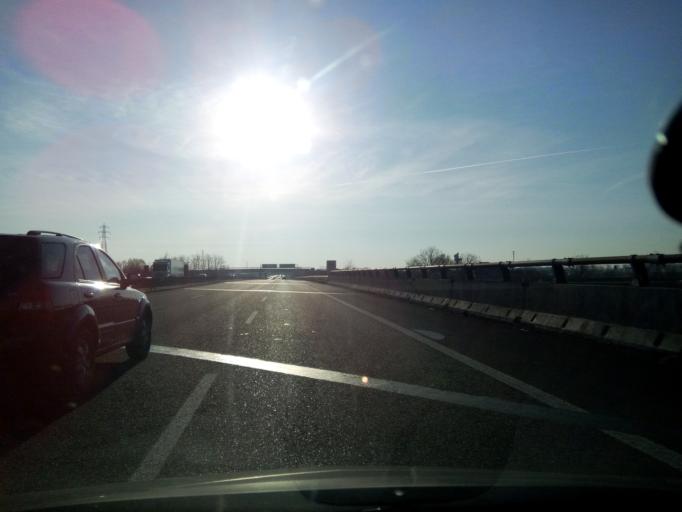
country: IT
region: Emilia-Romagna
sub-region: Provincia di Parma
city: Fidenza
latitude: 44.8900
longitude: 10.0841
